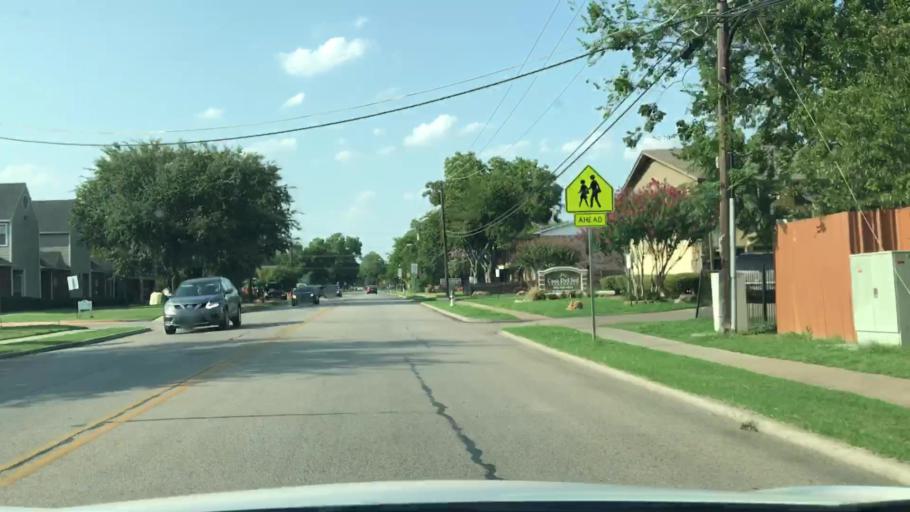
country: US
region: Texas
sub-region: Dallas County
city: Irving
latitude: 32.8204
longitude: -96.9342
